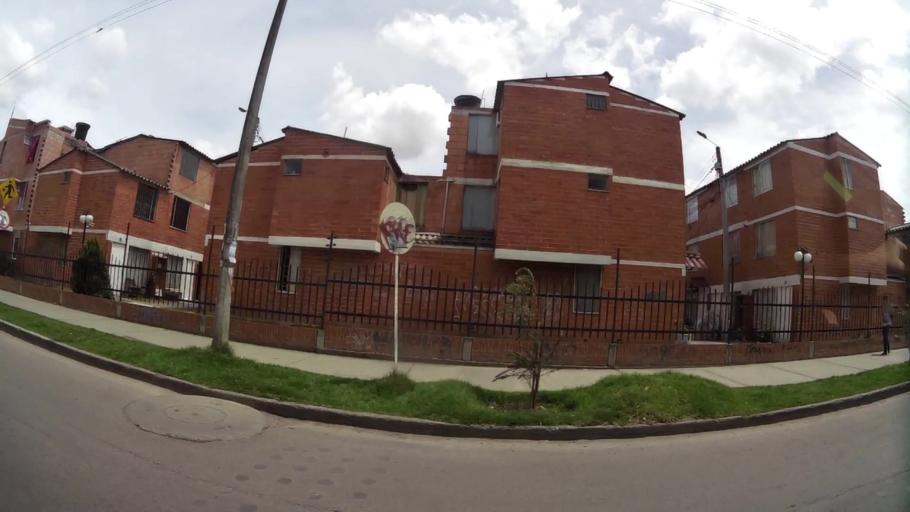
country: CO
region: Cundinamarca
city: Funza
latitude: 4.6516
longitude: -74.1614
